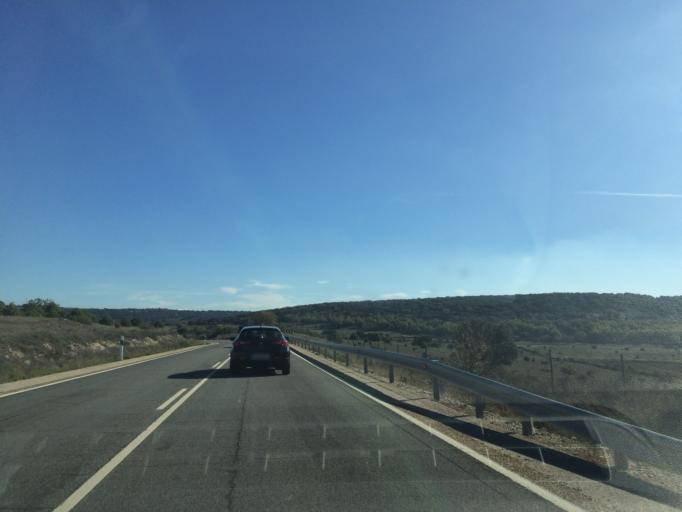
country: ES
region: Madrid
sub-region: Provincia de Madrid
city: Venturada
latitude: 40.7806
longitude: -3.6450
